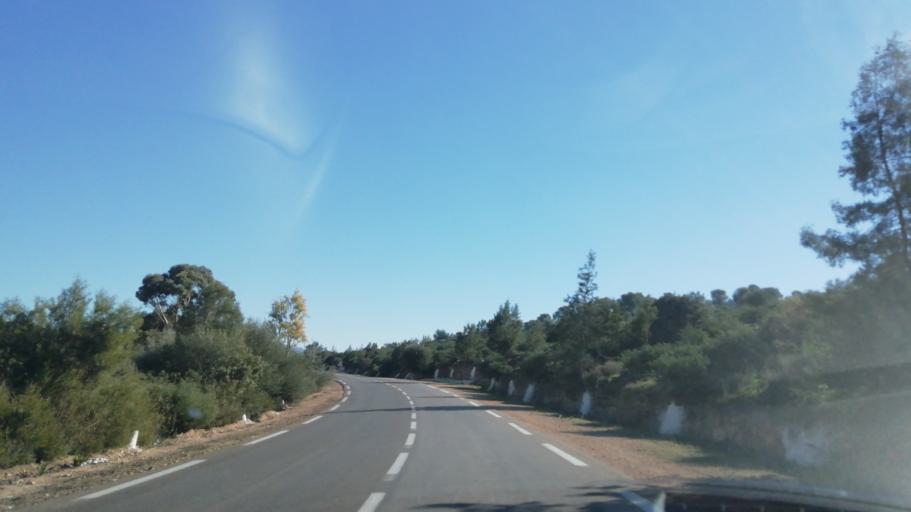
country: DZ
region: Tlemcen
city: Beni Mester
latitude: 34.8143
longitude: -1.6316
